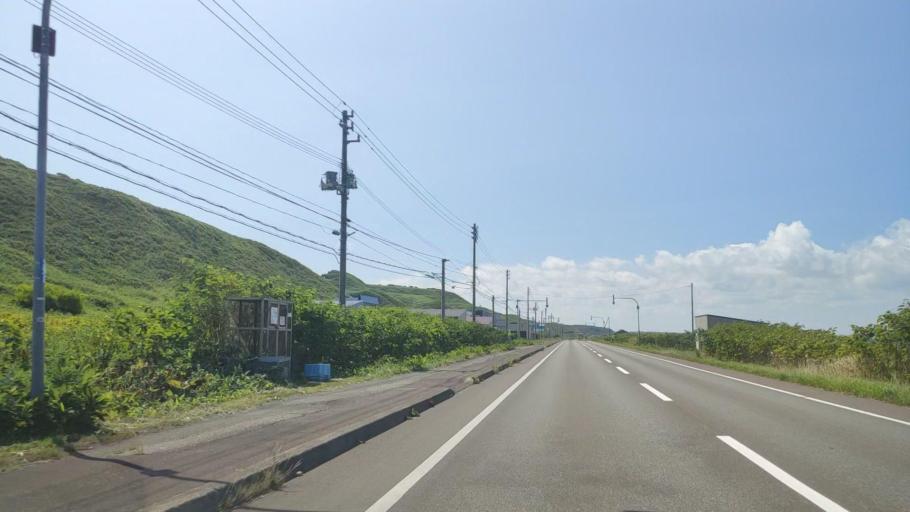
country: JP
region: Hokkaido
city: Makubetsu
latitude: 45.4464
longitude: 141.8691
